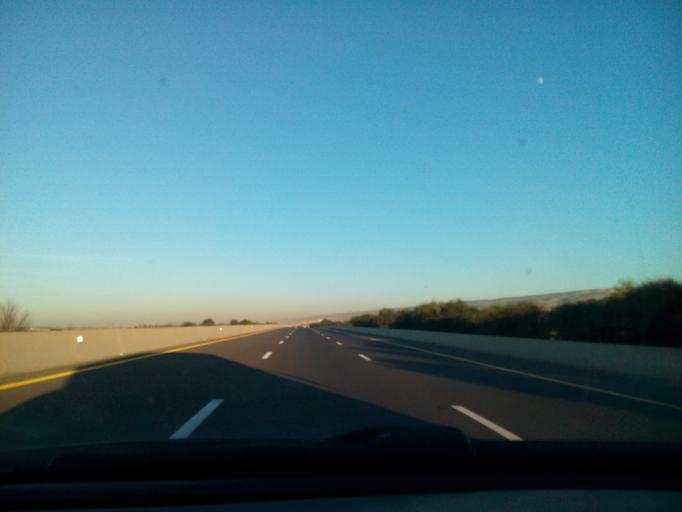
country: DZ
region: Relizane
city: Oued Rhiou
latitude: 35.9773
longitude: 0.9216
